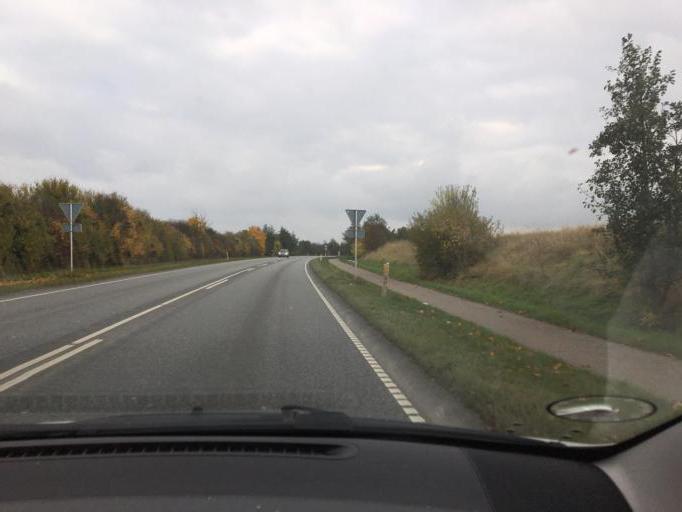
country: DK
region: South Denmark
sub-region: Fredericia Kommune
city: Fredericia
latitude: 55.6061
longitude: 9.7574
